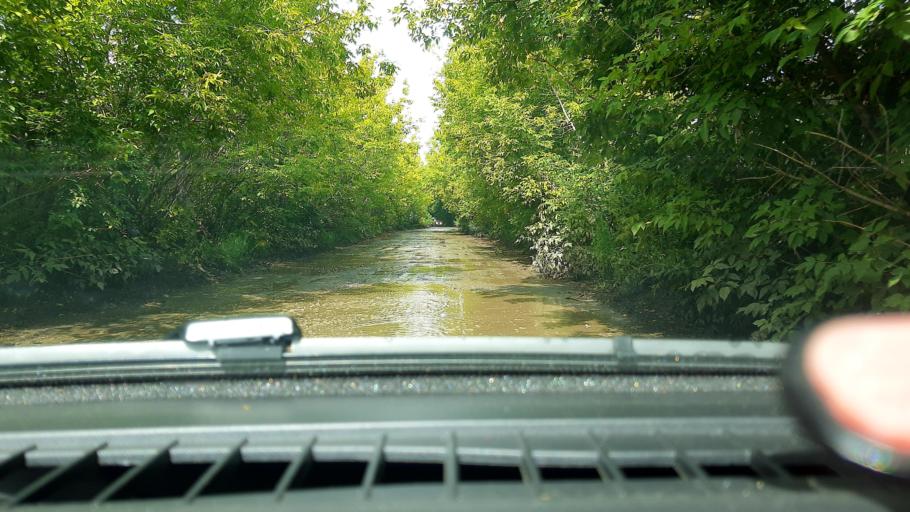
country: RU
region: Nizjnij Novgorod
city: Gorbatovka
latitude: 56.2546
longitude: 43.8325
